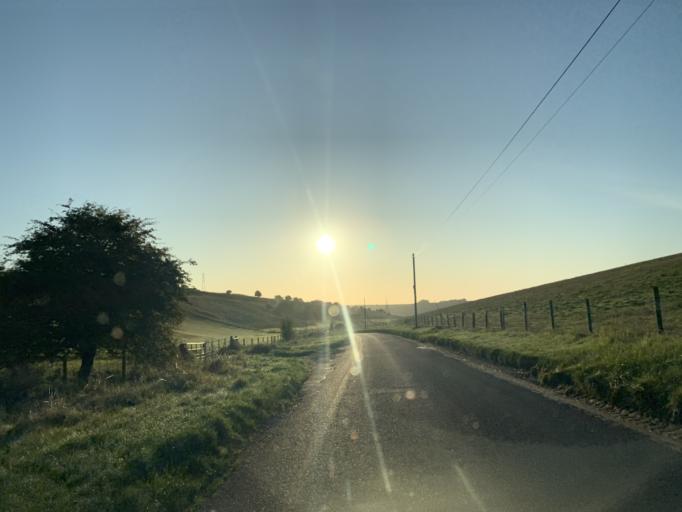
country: GB
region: England
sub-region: Wiltshire
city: Woodford
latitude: 51.1272
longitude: -1.8479
